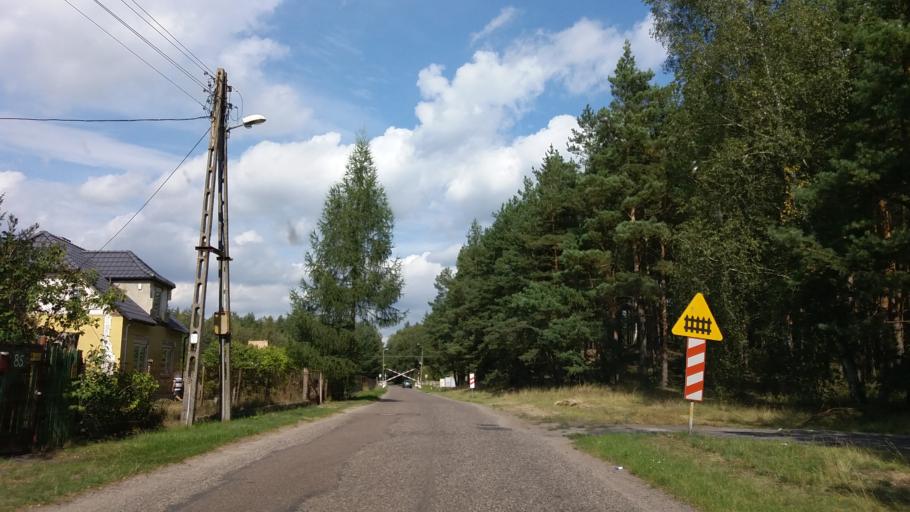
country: PL
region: West Pomeranian Voivodeship
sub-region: Powiat stargardzki
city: Kobylanka
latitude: 53.3691
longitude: 14.8805
